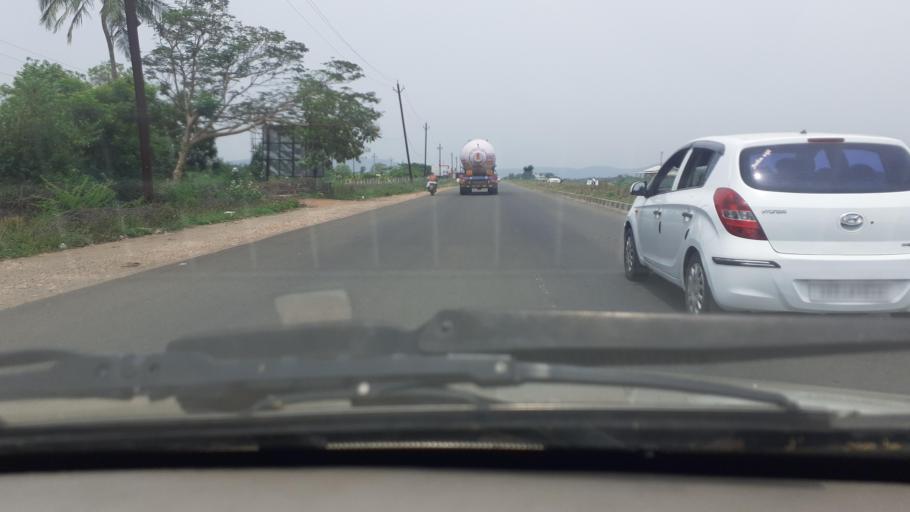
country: IN
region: Tamil Nadu
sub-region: Tirunelveli Kattabo
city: Tirunelveli
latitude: 8.7129
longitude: 77.7965
